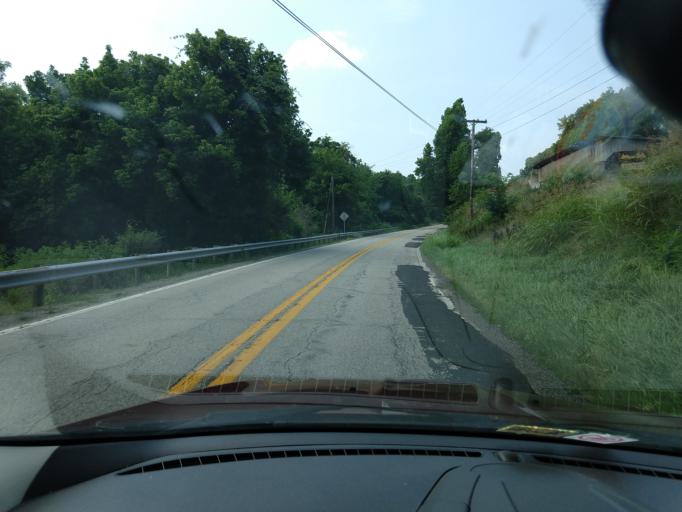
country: US
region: West Virginia
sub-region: Mason County
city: New Haven
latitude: 38.9249
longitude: -81.9127
